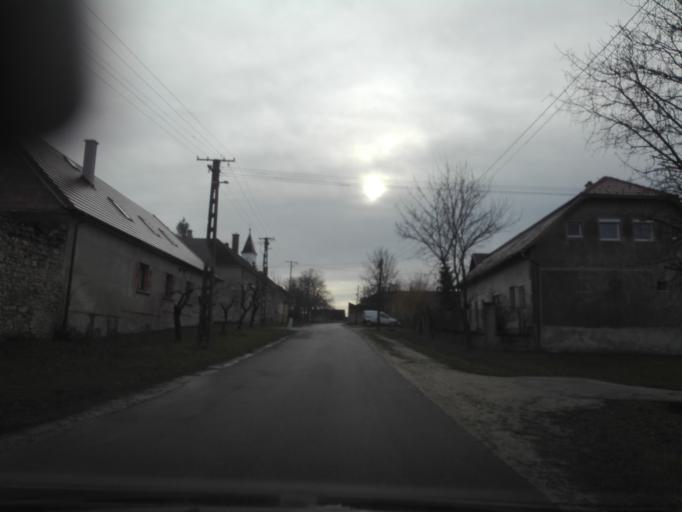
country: HU
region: Veszprem
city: Balatonfured
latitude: 47.0103
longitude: 17.7897
